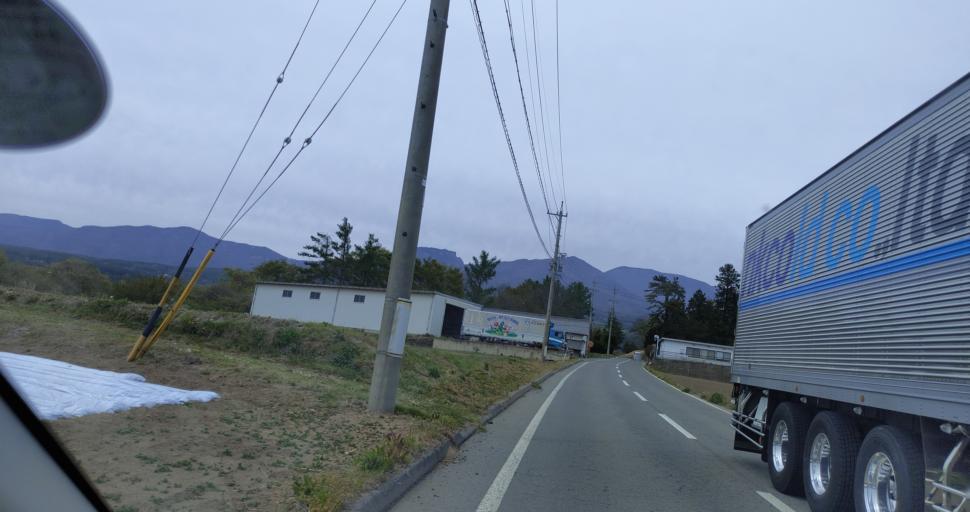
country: JP
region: Nagano
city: Komoro
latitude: 36.3272
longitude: 138.4883
